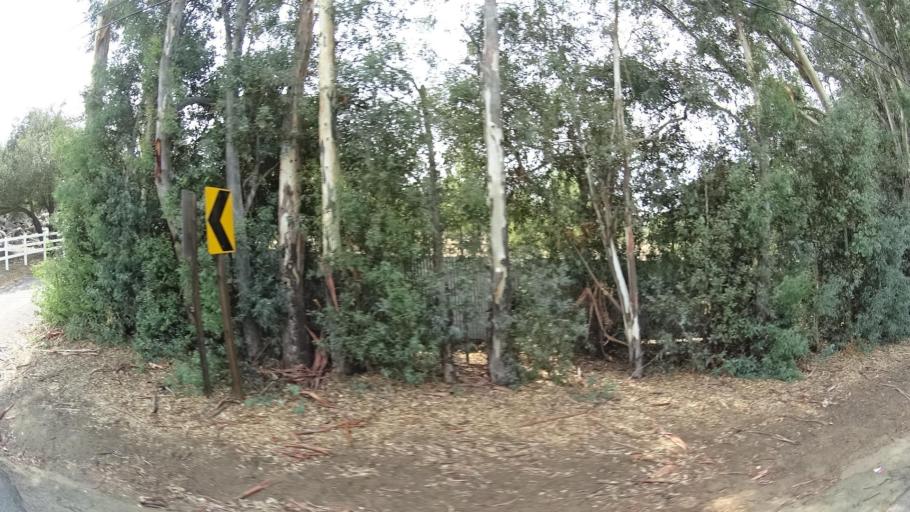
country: US
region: California
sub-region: San Diego County
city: Ramona
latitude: 33.0090
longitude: -116.9050
